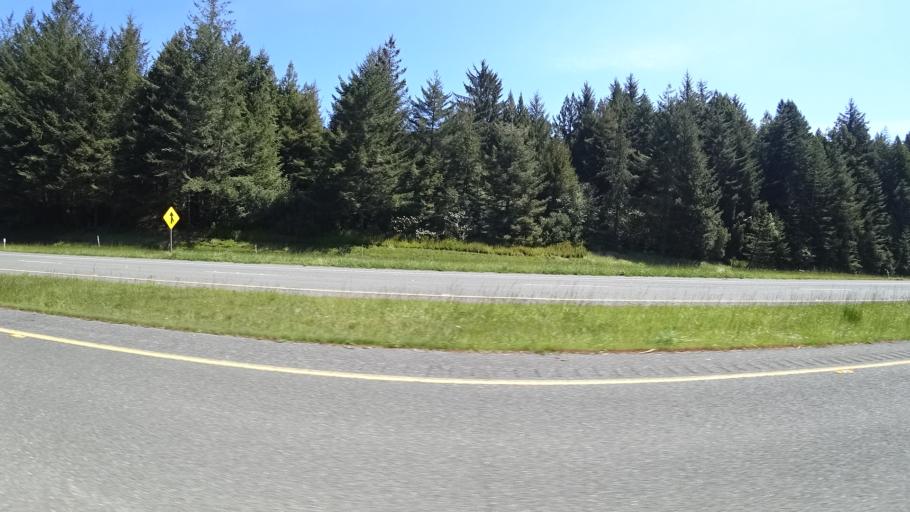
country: US
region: California
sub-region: Humboldt County
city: Westhaven-Moonstone
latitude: 41.0999
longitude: -124.1540
